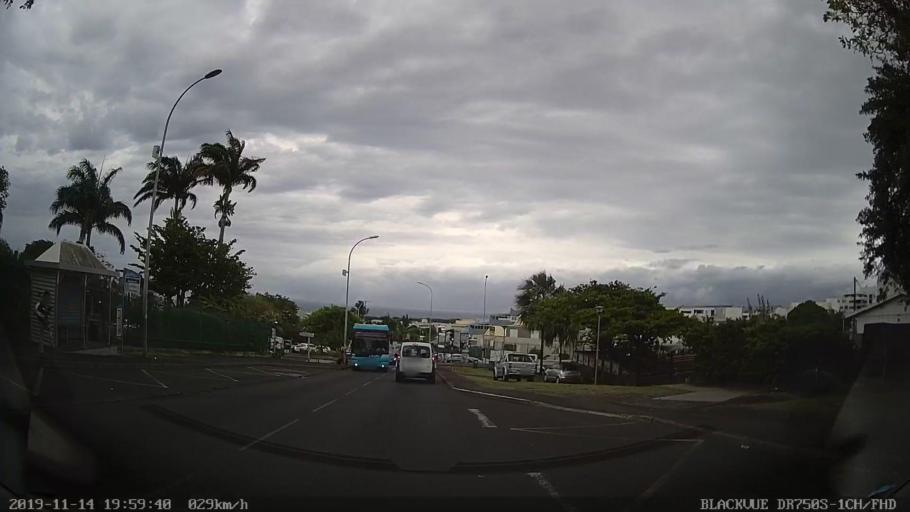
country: RE
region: Reunion
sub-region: Reunion
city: Saint-Denis
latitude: -20.9037
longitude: 55.4877
